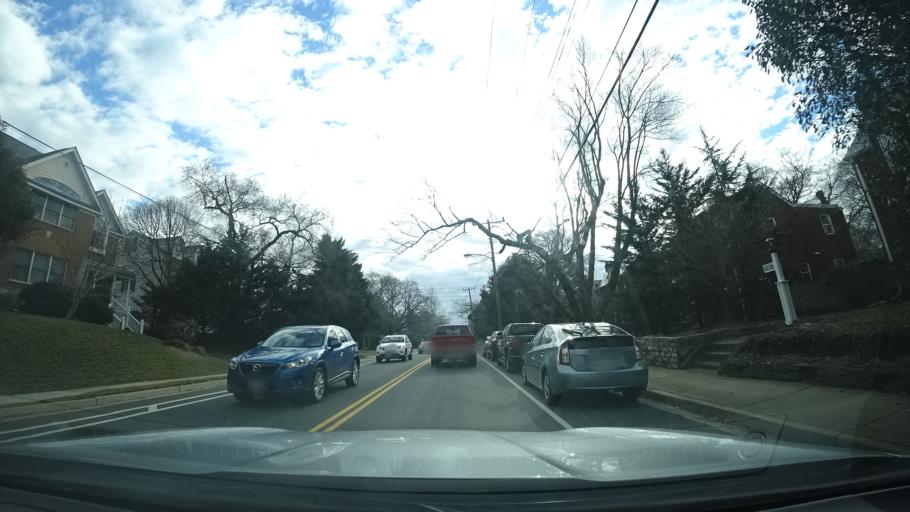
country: US
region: Virginia
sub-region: Fairfax County
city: Seven Corners
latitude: 38.8872
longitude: -77.1461
